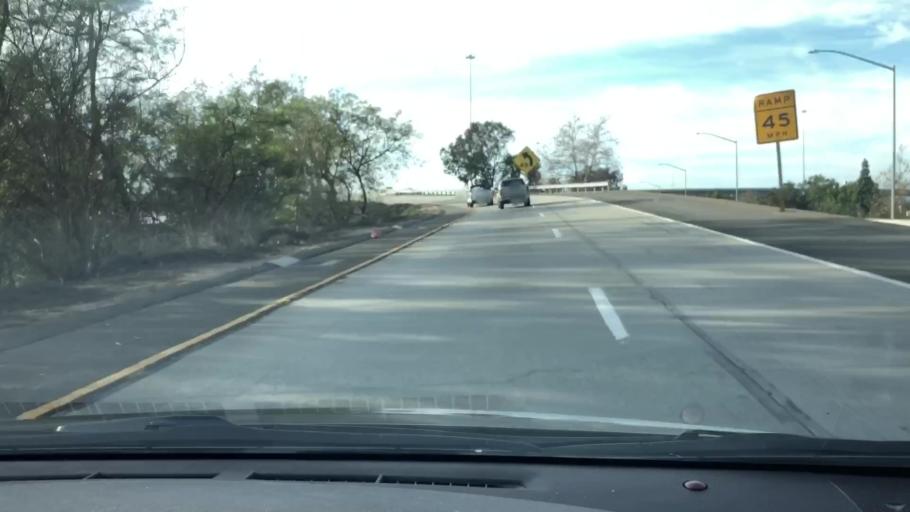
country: US
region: California
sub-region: Orange County
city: Placentia
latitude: 33.8491
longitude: -117.8730
